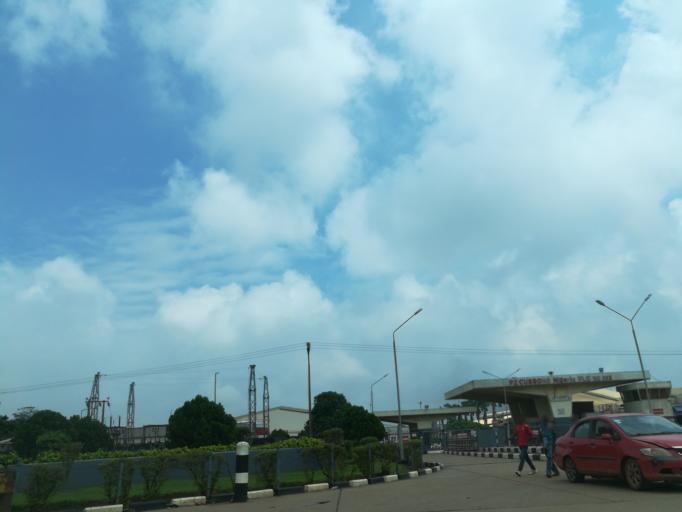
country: NG
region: Lagos
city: Ikorodu
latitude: 6.6746
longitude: 3.5127
